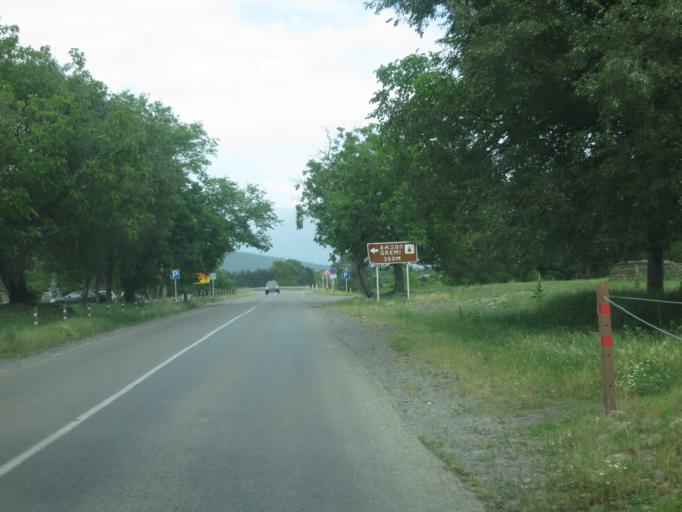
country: GE
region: Kakheti
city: Tsinandali
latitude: 41.9999
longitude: 45.6563
